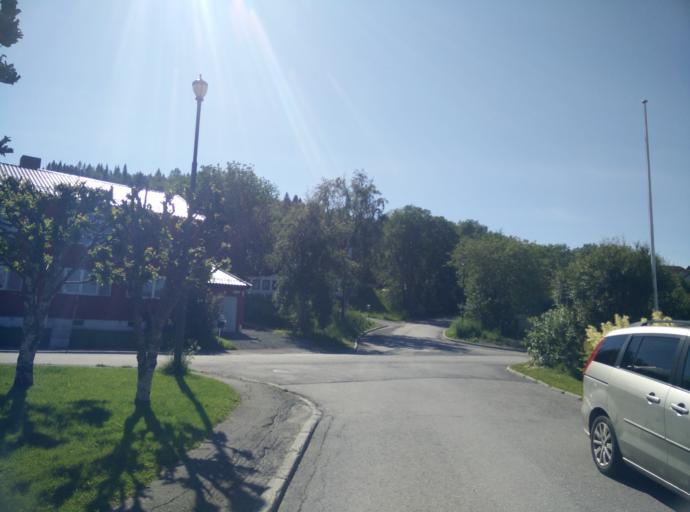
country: NO
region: Sor-Trondelag
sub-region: Trondheim
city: Trondheim
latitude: 63.4228
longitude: 10.3554
